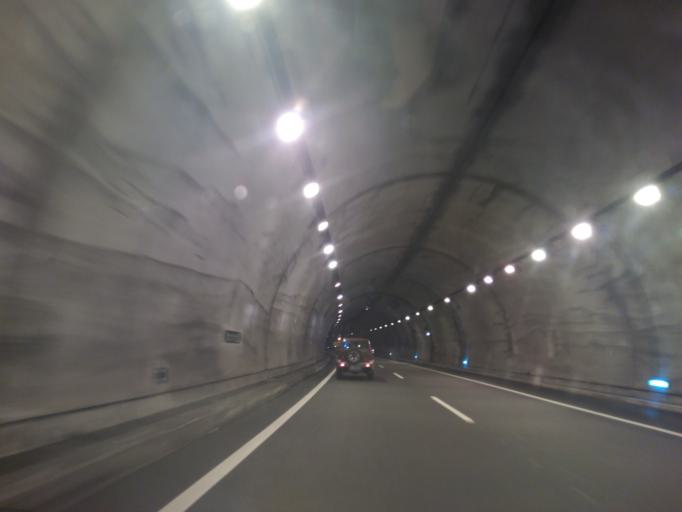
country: ES
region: Cantabria
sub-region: Provincia de Cantabria
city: Los Corrales de Buelna
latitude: 43.2467
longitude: -4.0824
